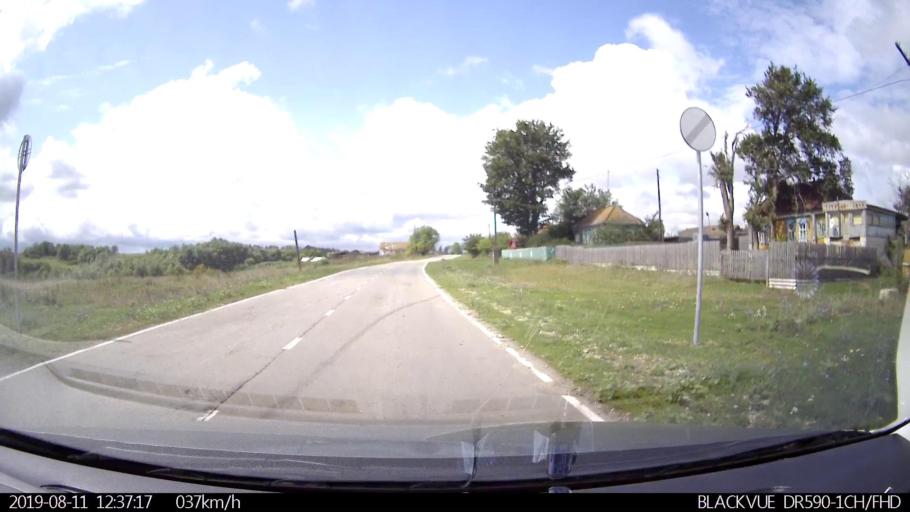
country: RU
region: Ulyanovsk
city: Ignatovka
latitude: 53.8239
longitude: 47.8168
